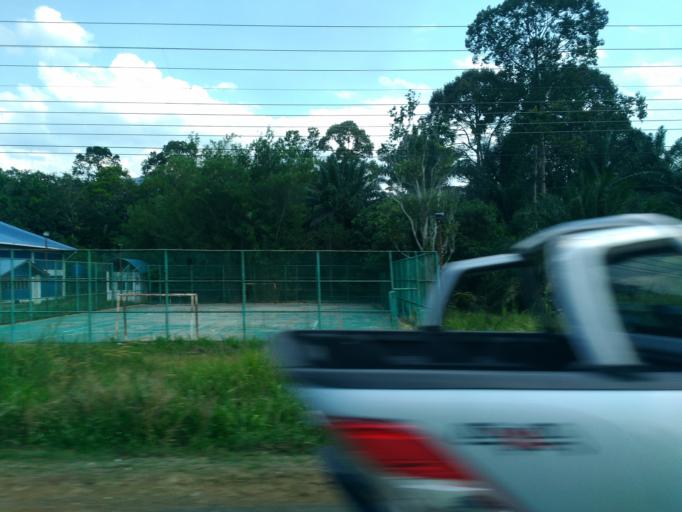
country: MY
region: Sabah
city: Ranau
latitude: 5.6243
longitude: 117.0980
